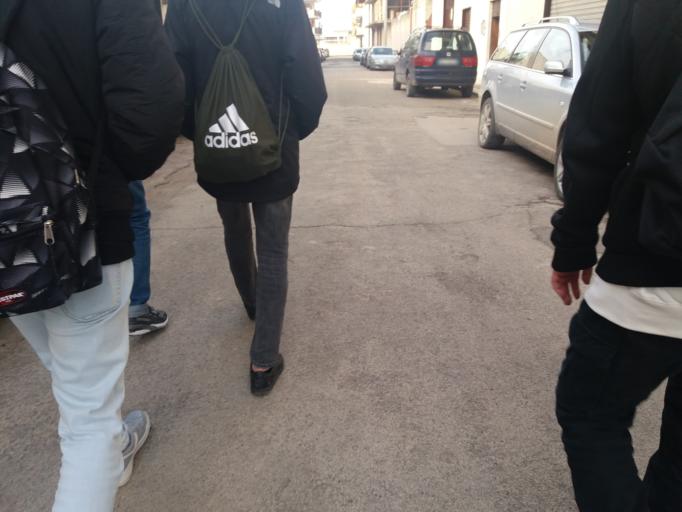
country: IT
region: Apulia
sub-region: Provincia di Barletta - Andria - Trani
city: Andria
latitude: 41.2407
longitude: 16.2896
